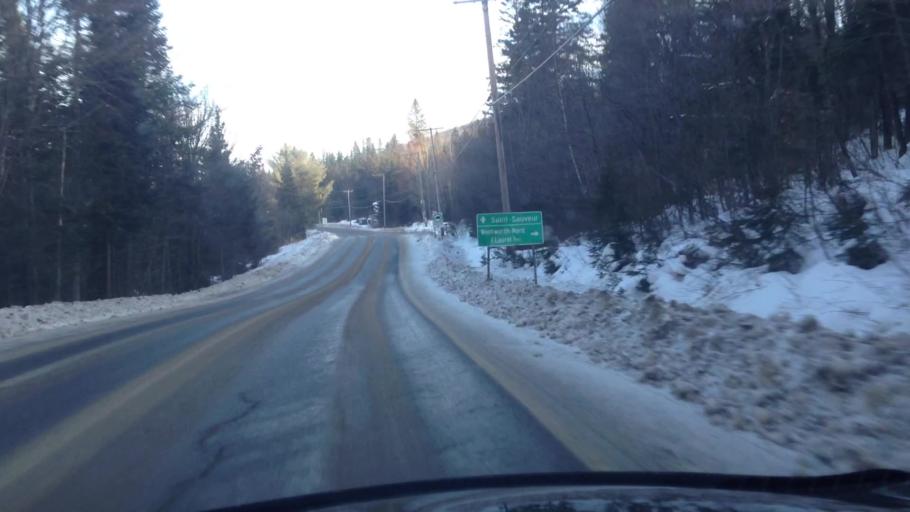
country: CA
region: Quebec
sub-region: Laurentides
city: Sainte-Agathe-des-Monts
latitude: 45.9105
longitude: -74.3455
